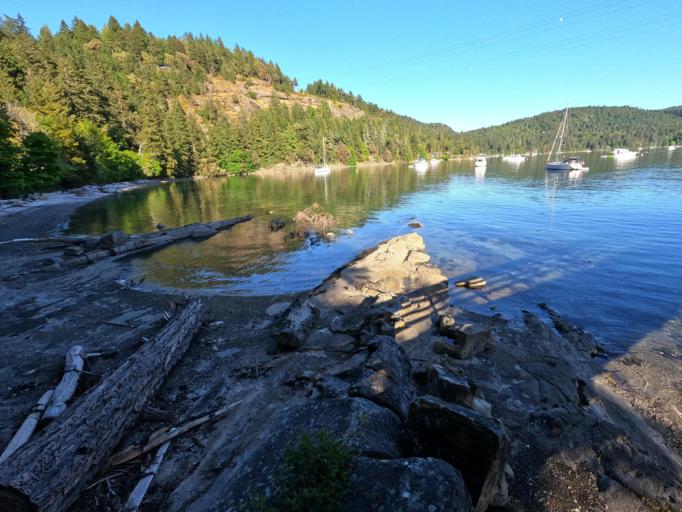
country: CA
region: British Columbia
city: North Saanich
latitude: 48.8974
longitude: -123.4027
